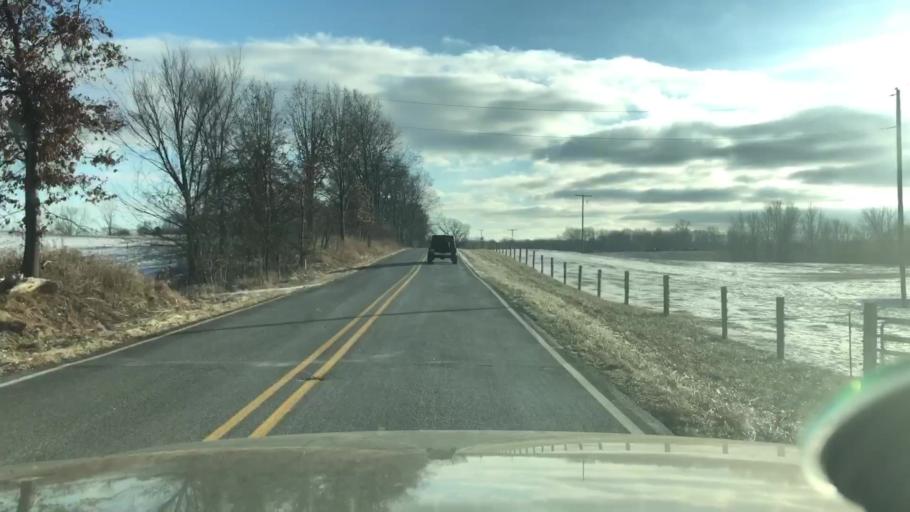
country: US
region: Michigan
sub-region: Jackson County
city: Vandercook Lake
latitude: 42.1020
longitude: -84.4511
